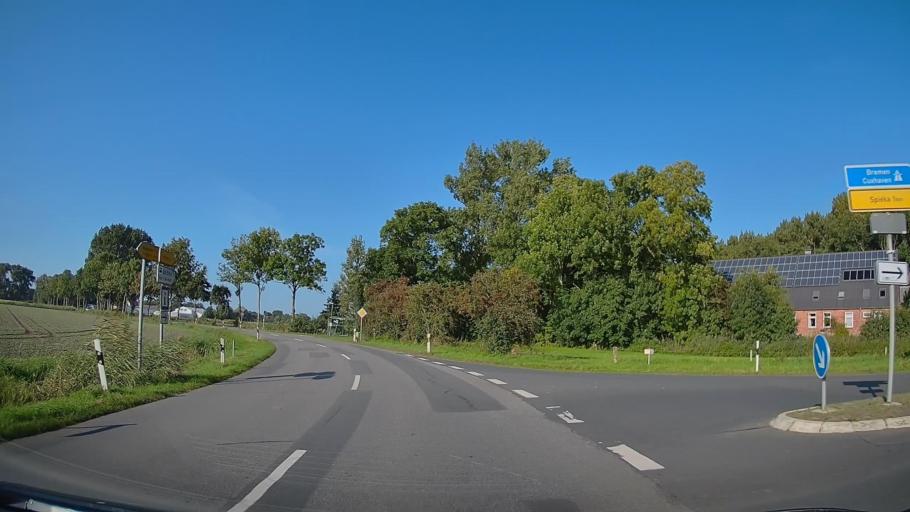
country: DE
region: Lower Saxony
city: Cappel
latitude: 53.7521
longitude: 8.5645
